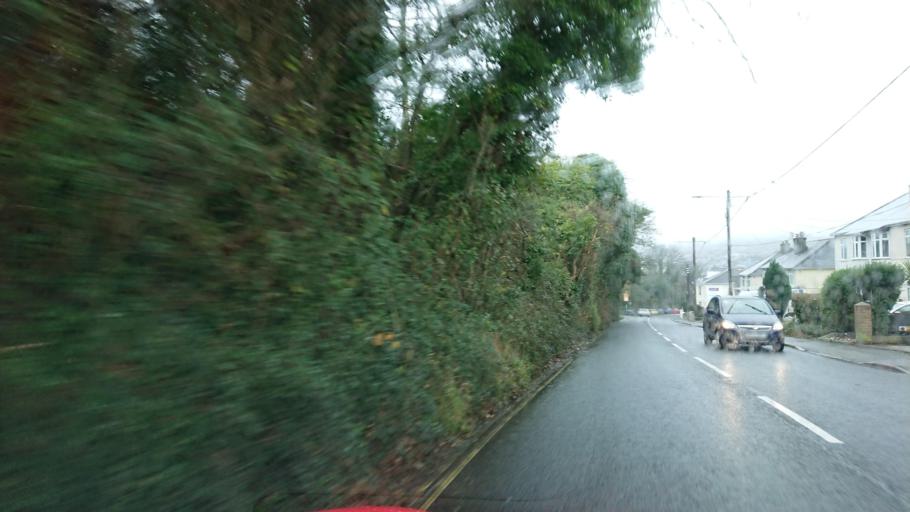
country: GB
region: England
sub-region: Plymouth
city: Plymstock
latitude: 50.3524
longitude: -4.1080
